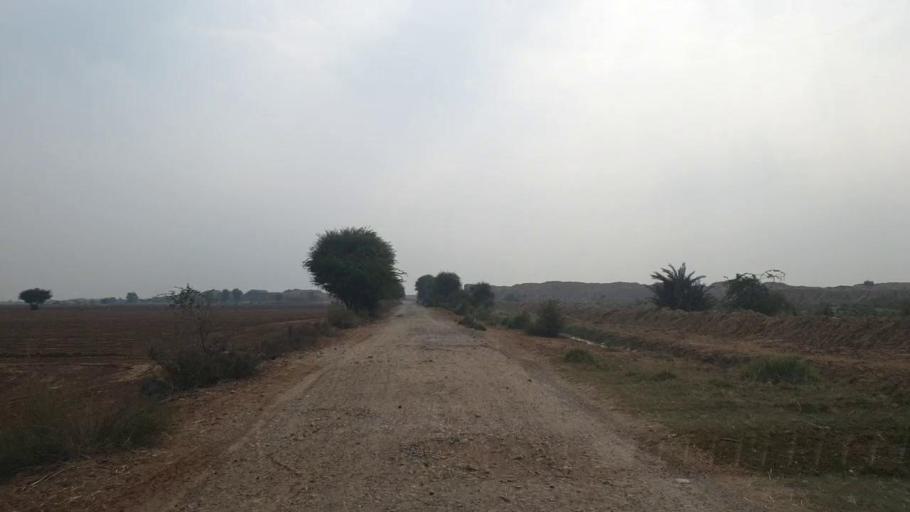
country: PK
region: Sindh
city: Sann
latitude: 26.0189
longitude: 68.1440
